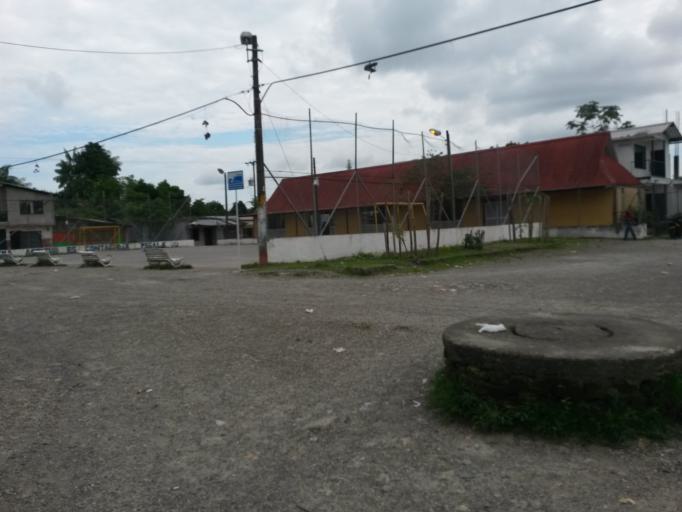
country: CO
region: Cauca
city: Guapi
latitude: 2.5714
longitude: -77.8879
